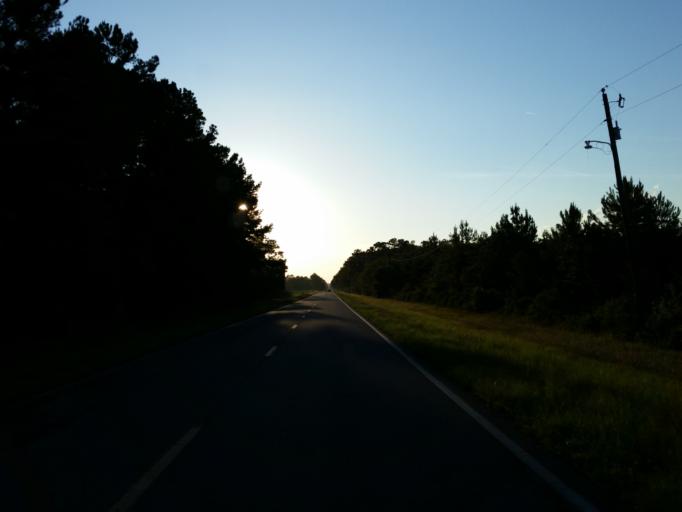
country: US
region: Georgia
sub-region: Lanier County
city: Lakeland
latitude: 31.1693
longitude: -83.1034
